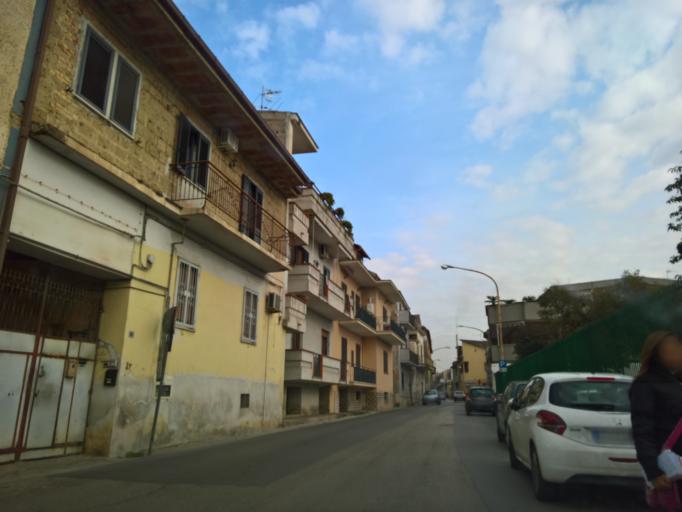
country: IT
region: Campania
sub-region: Provincia di Caserta
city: San Prisco
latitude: 41.0879
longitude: 14.2745
